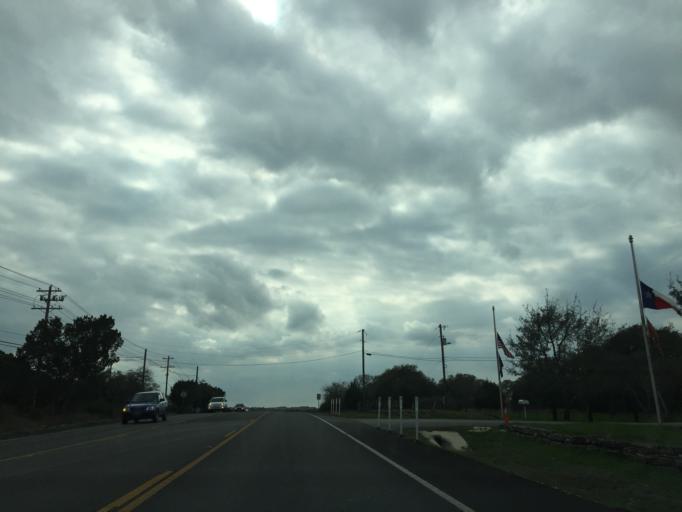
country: US
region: Texas
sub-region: Travis County
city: Shady Hollow
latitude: 30.1663
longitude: -97.9454
